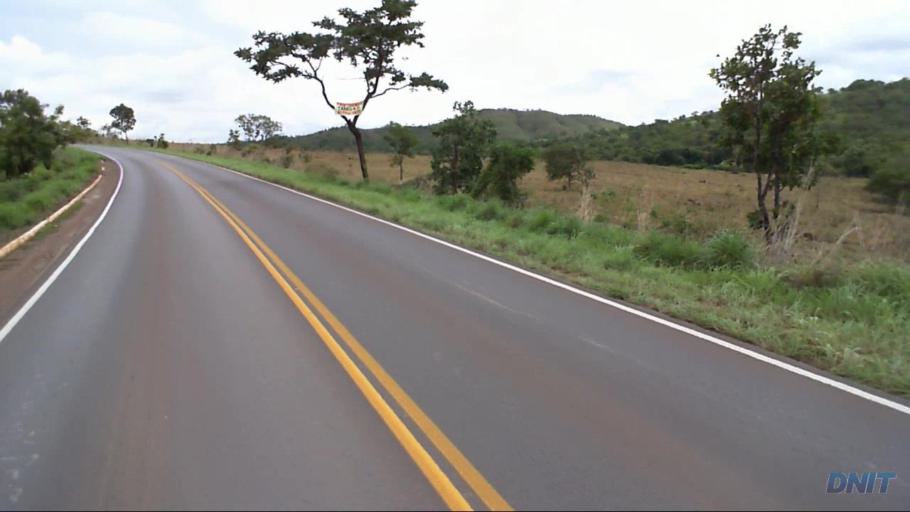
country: BR
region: Goias
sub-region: Padre Bernardo
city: Padre Bernardo
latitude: -15.4343
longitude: -48.1929
